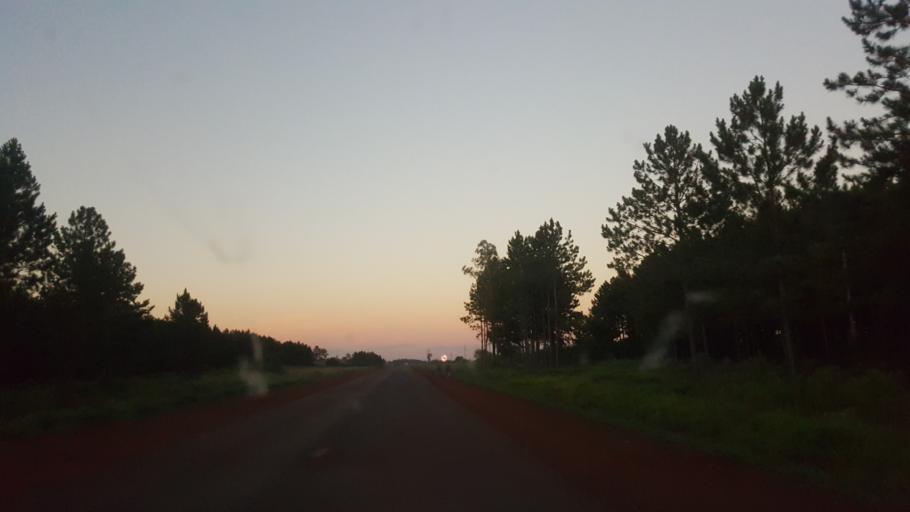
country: AR
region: Corrientes
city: Garruchos
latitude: -28.2211
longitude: -55.7973
